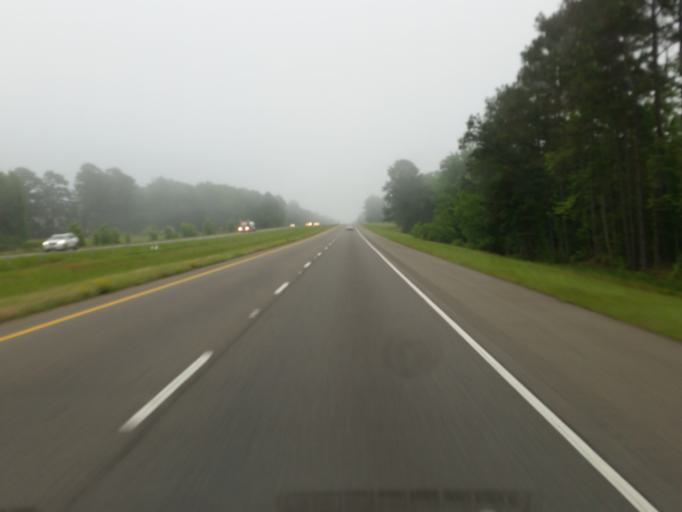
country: US
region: Louisiana
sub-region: Bossier Parish
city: Haughton
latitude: 32.5805
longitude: -93.4141
